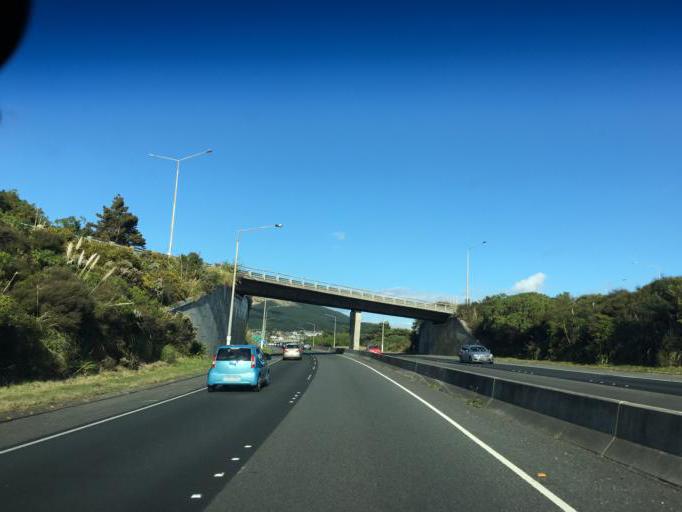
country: NZ
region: Wellington
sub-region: Porirua City
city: Porirua
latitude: -41.1309
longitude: 174.8443
